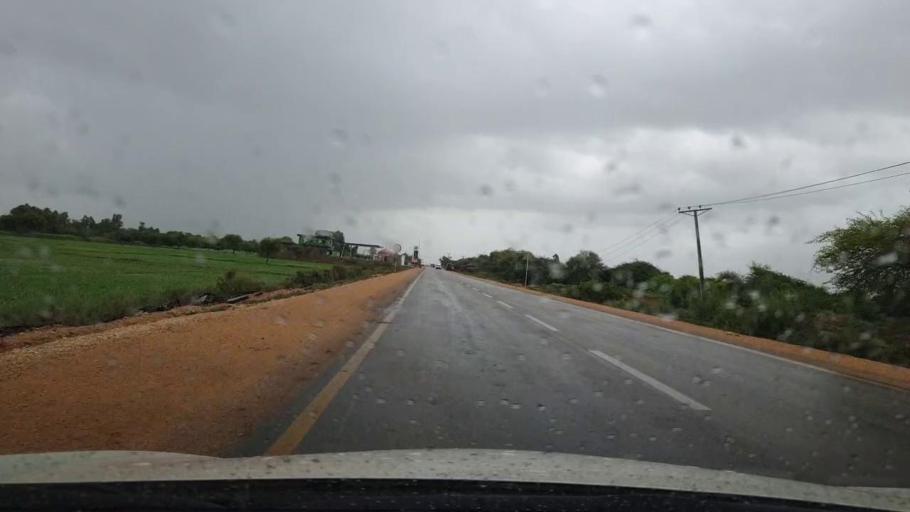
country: PK
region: Sindh
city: Badin
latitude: 24.6530
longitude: 68.6741
